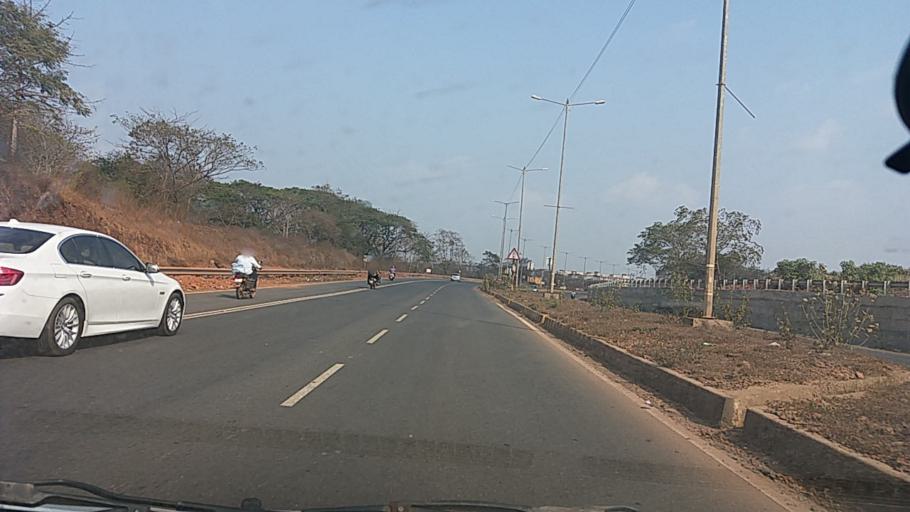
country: IN
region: Goa
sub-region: North Goa
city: Goa Velha
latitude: 15.4897
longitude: 73.8954
